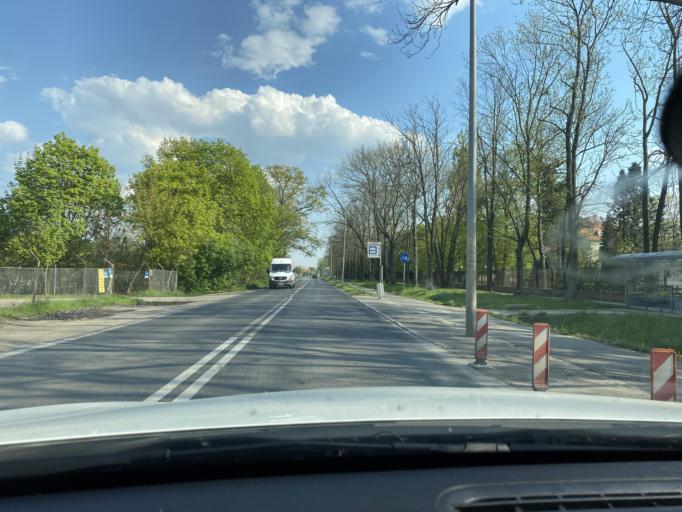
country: PL
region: Lower Silesian Voivodeship
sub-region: Powiat trzebnicki
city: Psary
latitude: 51.1509
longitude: 17.0177
